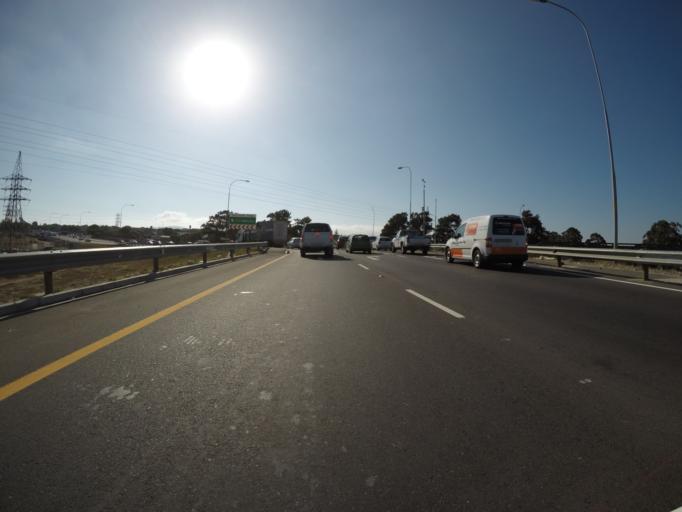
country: ZA
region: Western Cape
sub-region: City of Cape Town
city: Kraaifontein
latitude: -33.8873
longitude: 18.6745
